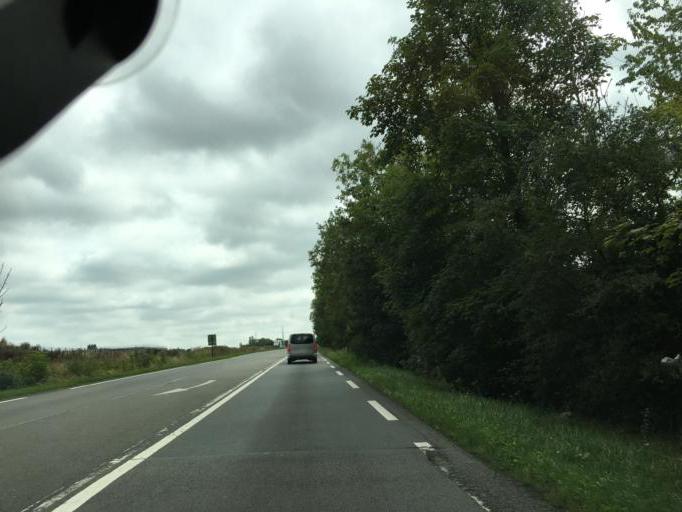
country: FR
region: Nord-Pas-de-Calais
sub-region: Departement du Pas-de-Calais
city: Houdain
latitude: 50.4650
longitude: 2.5336
